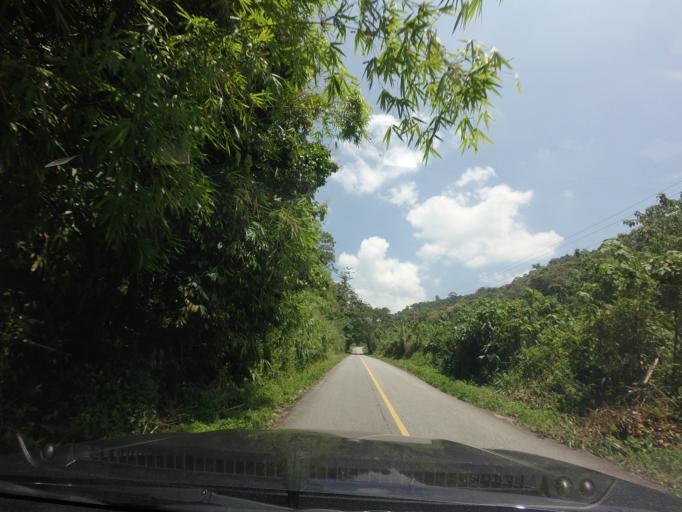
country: TH
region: Loei
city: Na Haeo
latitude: 17.6438
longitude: 100.9090
